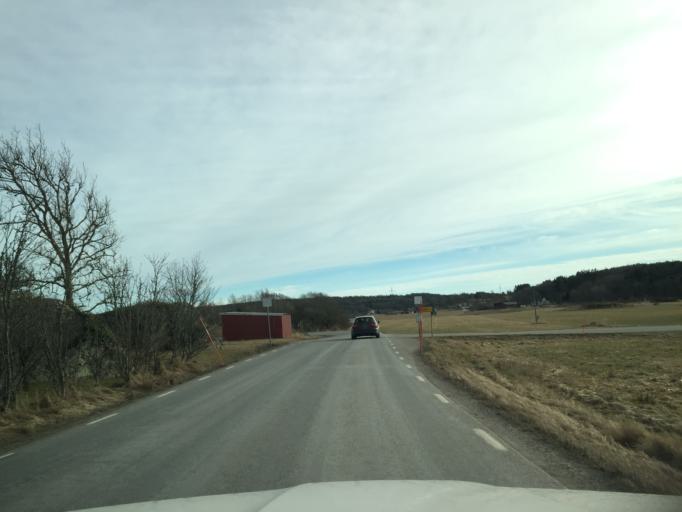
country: SE
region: Vaestra Goetaland
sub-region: Tjorns Kommun
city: Skaerhamn
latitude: 58.0269
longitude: 11.6053
